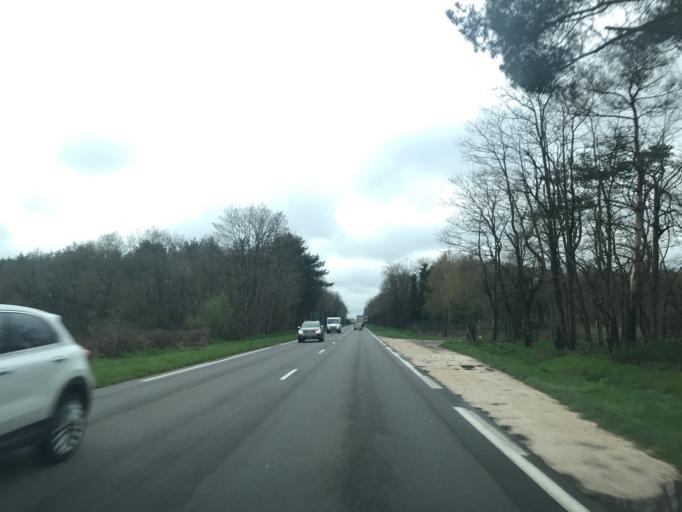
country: FR
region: Centre
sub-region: Departement du Loiret
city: Bray-en-Val
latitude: 47.8396
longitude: 2.3393
